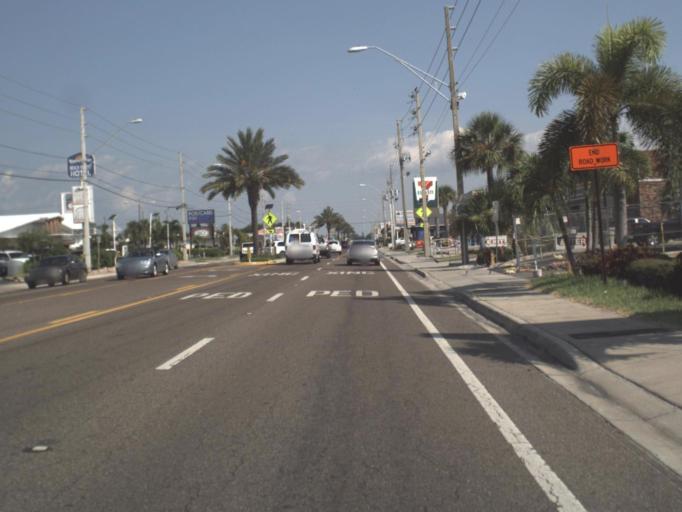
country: US
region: Florida
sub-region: Pinellas County
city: Saint Pete Beach
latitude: 27.7334
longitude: -82.7455
